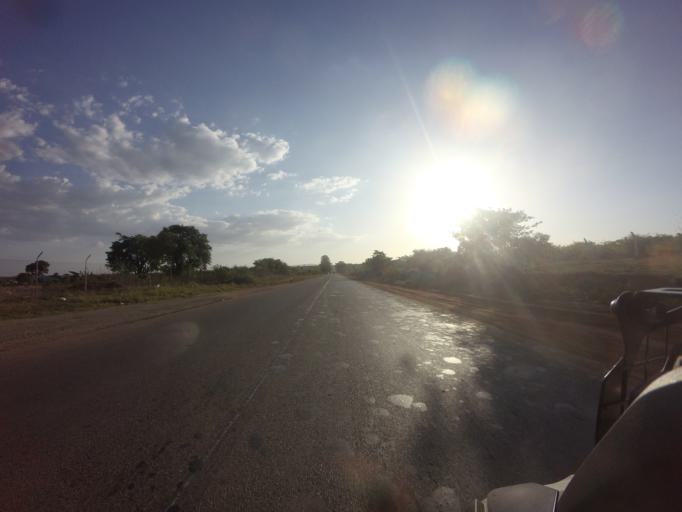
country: AO
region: Huila
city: Lubango
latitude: -14.8193
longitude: 13.6333
